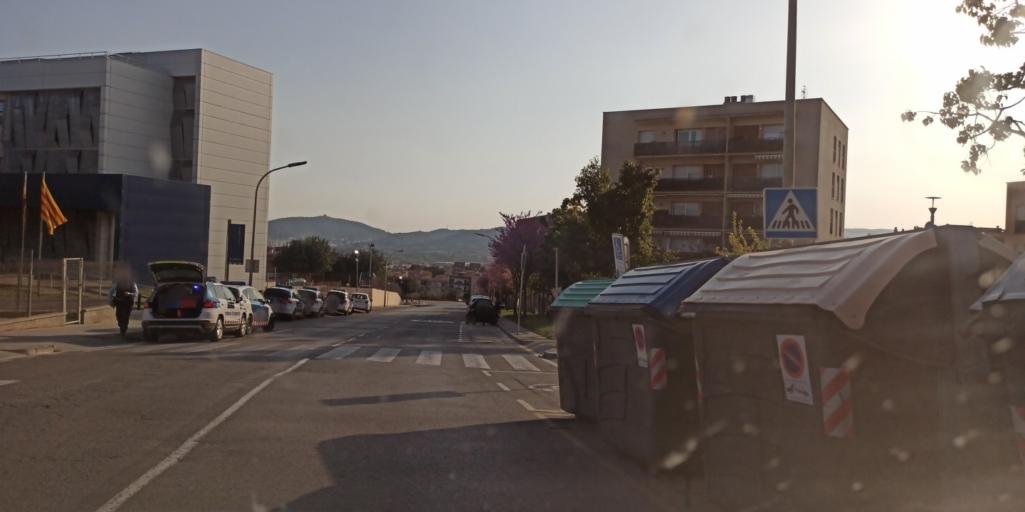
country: ES
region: Catalonia
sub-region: Provincia de Barcelona
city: Sant Feliu de Llobregat
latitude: 41.3908
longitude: 2.0488
